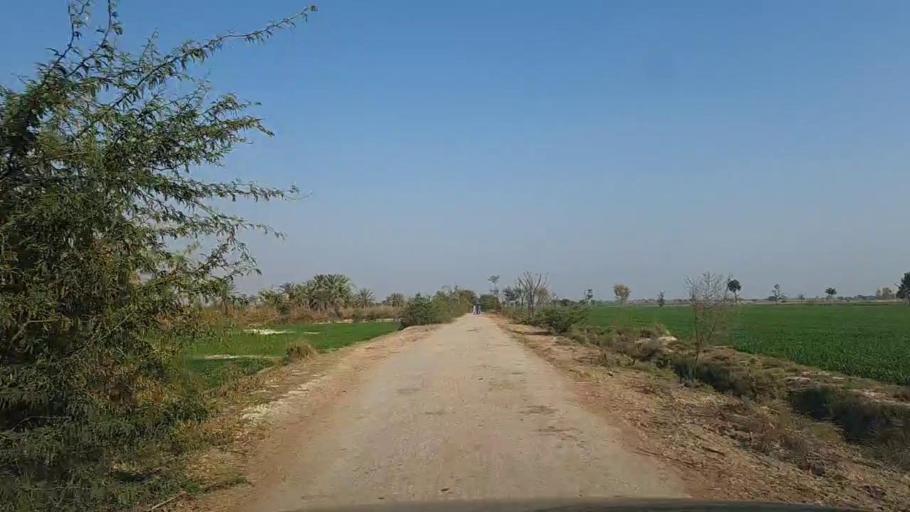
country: PK
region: Sindh
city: Nawabshah
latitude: 26.3873
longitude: 68.4611
